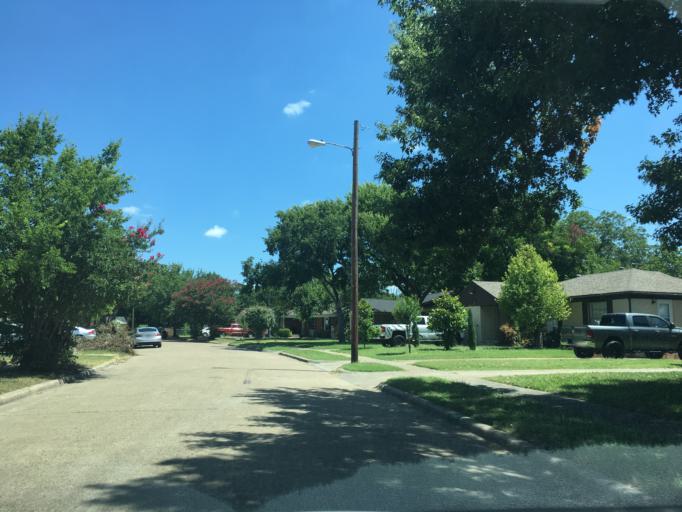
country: US
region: Texas
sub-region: Dallas County
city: Garland
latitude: 32.8394
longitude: -96.6817
